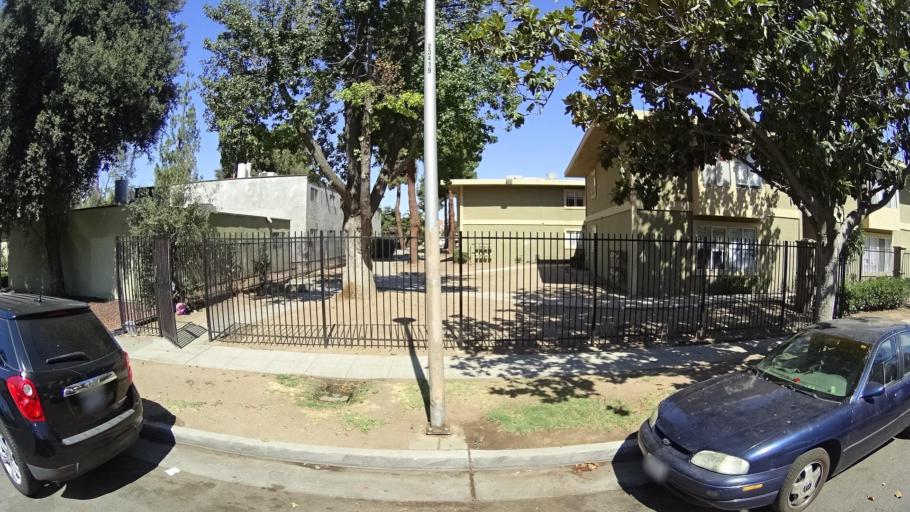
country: US
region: California
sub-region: Fresno County
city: Fresno
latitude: 36.7412
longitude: -119.7757
